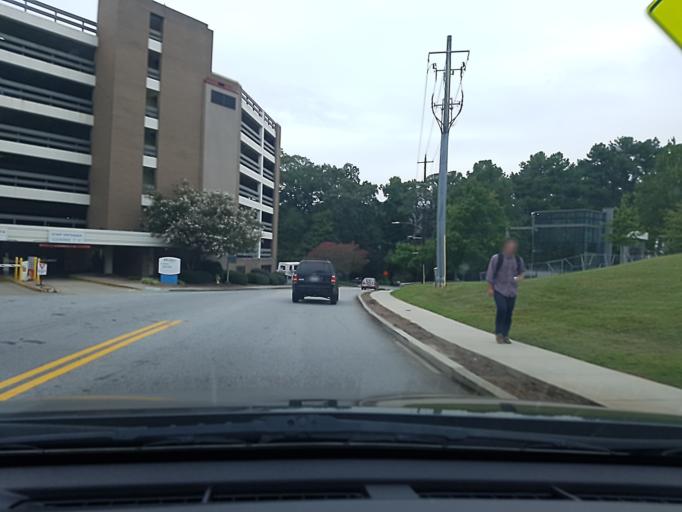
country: US
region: Georgia
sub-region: DeKalb County
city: North Decatur
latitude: 33.7942
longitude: -84.3186
